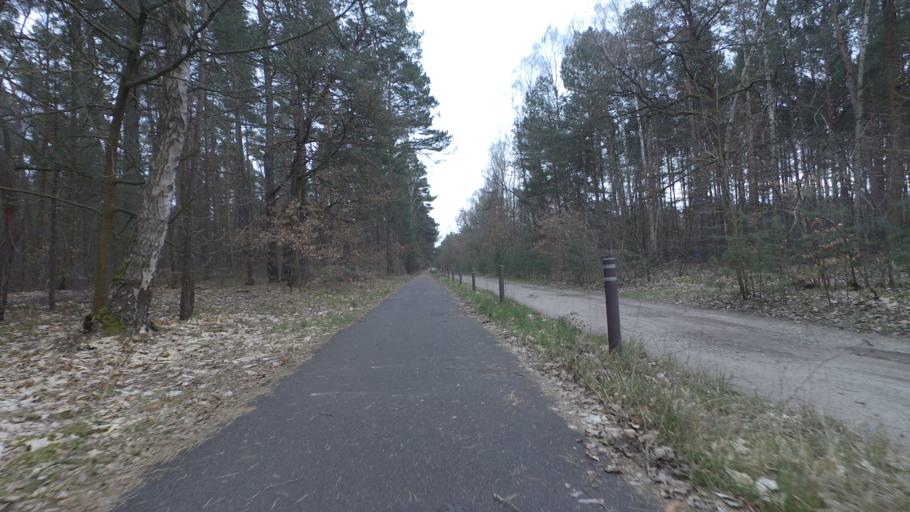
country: DE
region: Brandenburg
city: Lindow
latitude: 52.9913
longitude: 12.9616
